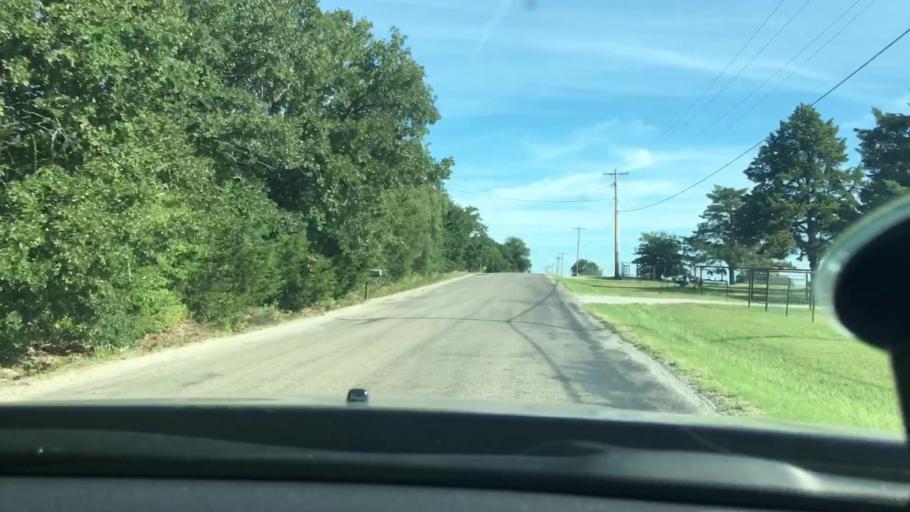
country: US
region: Oklahoma
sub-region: Carter County
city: Lone Grove
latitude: 34.2211
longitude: -97.2475
